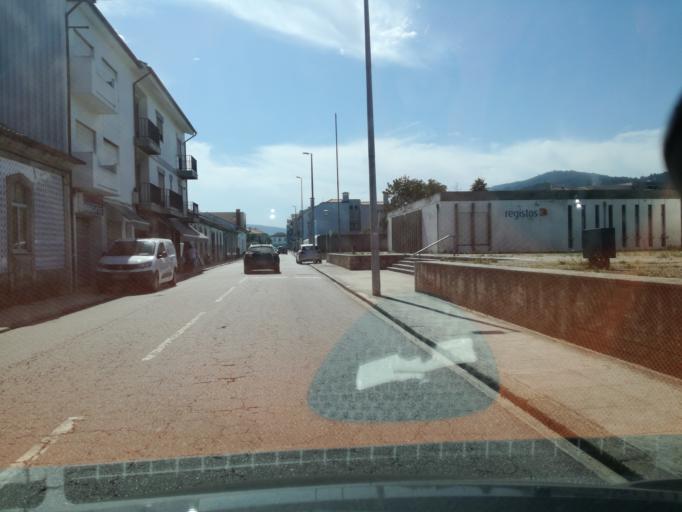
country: ES
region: Galicia
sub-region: Provincia de Pontevedra
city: A Guarda
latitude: 41.8768
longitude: -8.8368
